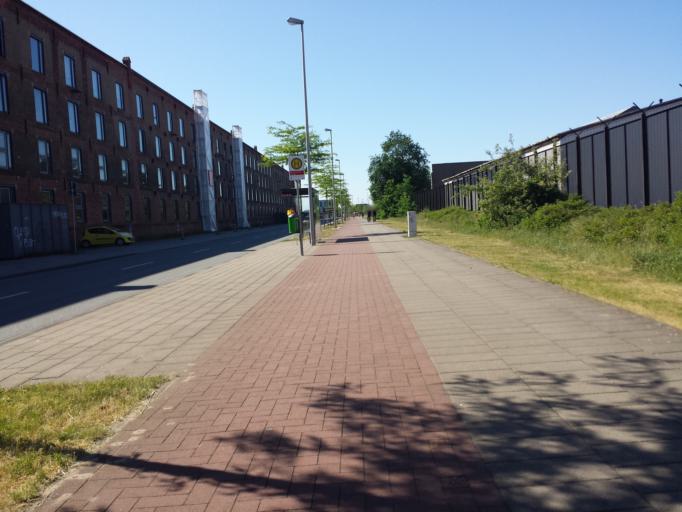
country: DE
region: Bremen
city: Bremen
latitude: 53.0976
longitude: 8.7700
